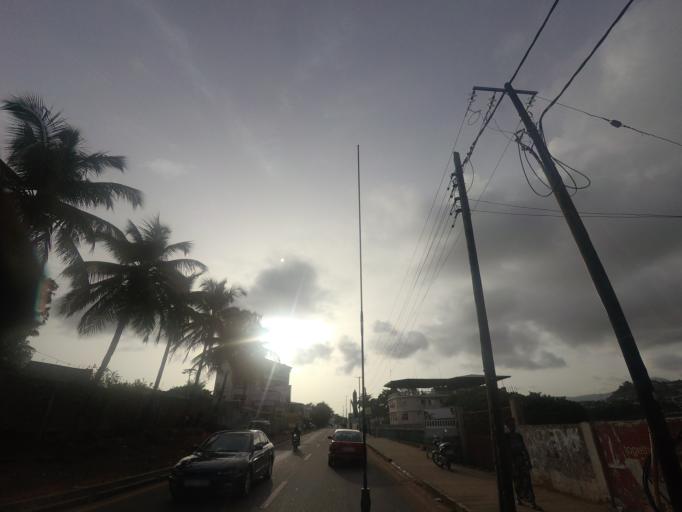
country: SL
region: Western Area
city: Freetown
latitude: 8.4925
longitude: -13.2795
